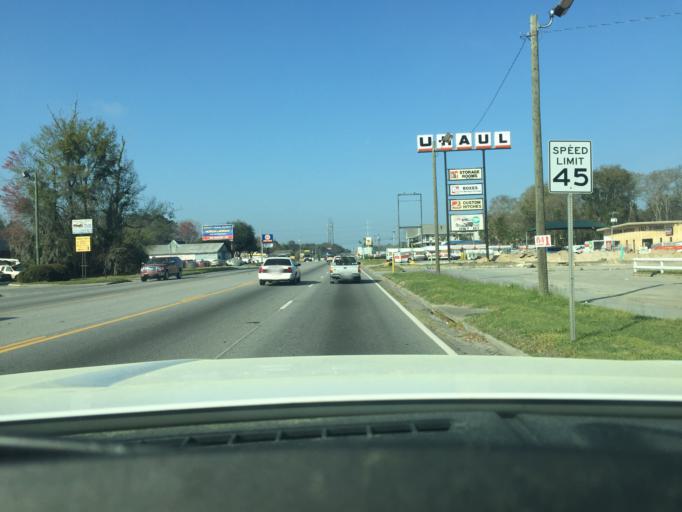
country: US
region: Georgia
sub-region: Chatham County
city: Savannah
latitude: 32.0526
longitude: -81.1471
